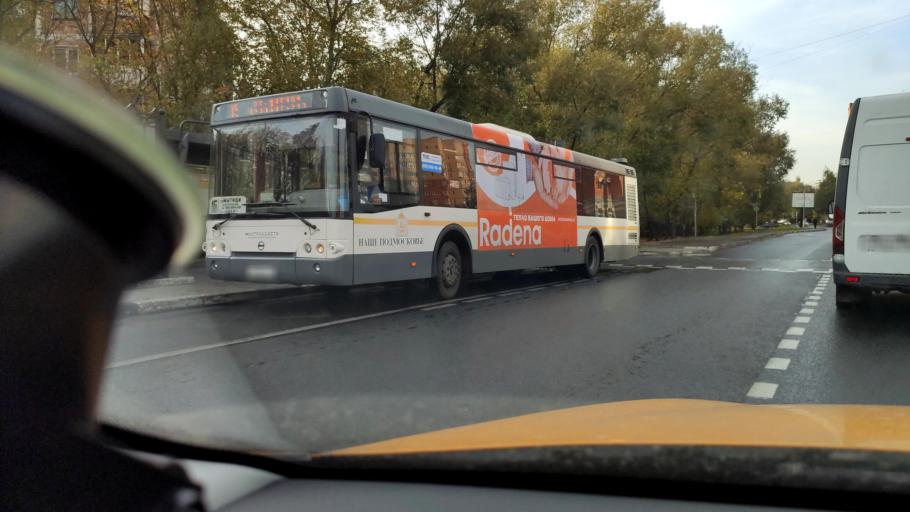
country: RU
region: Moskovskaya
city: Mytishchi
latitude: 55.9174
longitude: 37.7326
